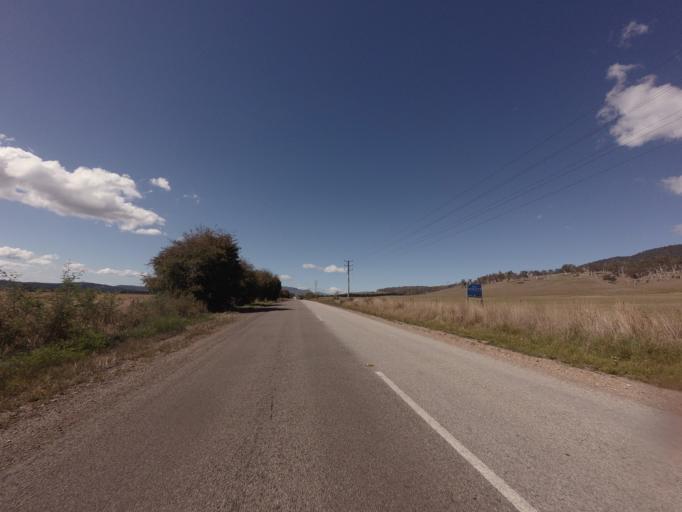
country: AU
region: Tasmania
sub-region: Break O'Day
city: St Helens
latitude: -41.6250
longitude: 147.9947
